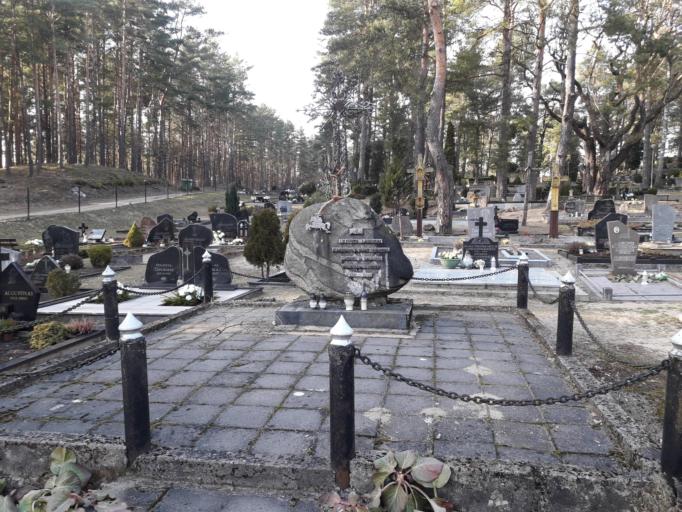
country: LT
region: Alytaus apskritis
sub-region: Alytaus rajonas
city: Daugai
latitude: 54.1660
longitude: 24.1820
